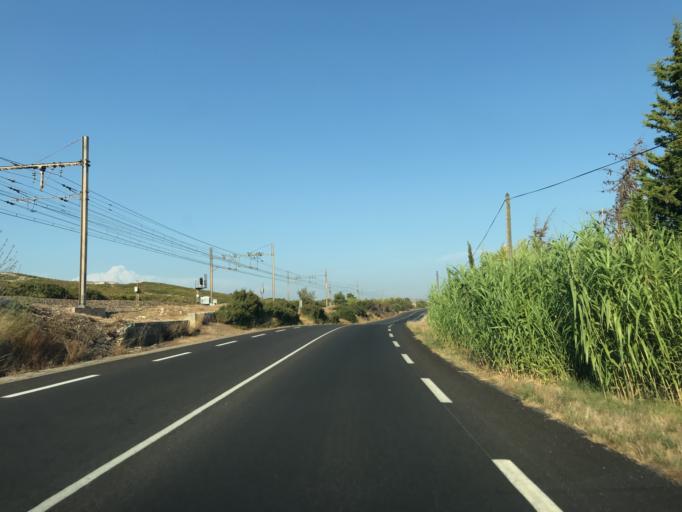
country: FR
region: Provence-Alpes-Cote d'Azur
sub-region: Departement des Bouches-du-Rhone
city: Cornillon-Confoux
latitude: 43.5317
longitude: 5.1054
